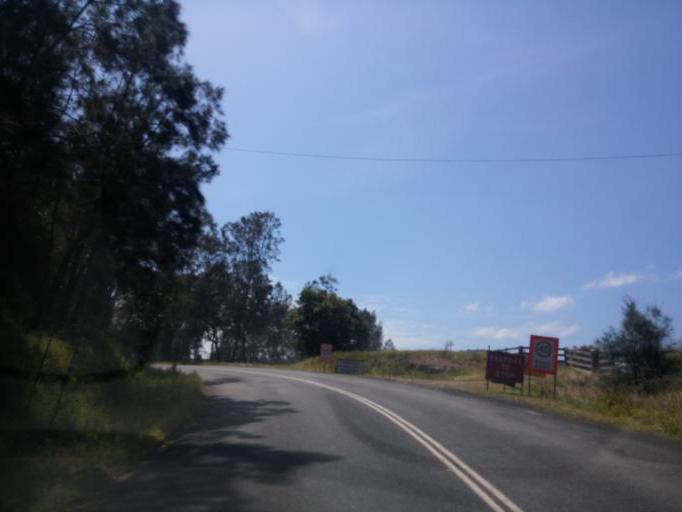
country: AU
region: New South Wales
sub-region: Great Lakes
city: Forster
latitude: -32.3931
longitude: 152.4399
